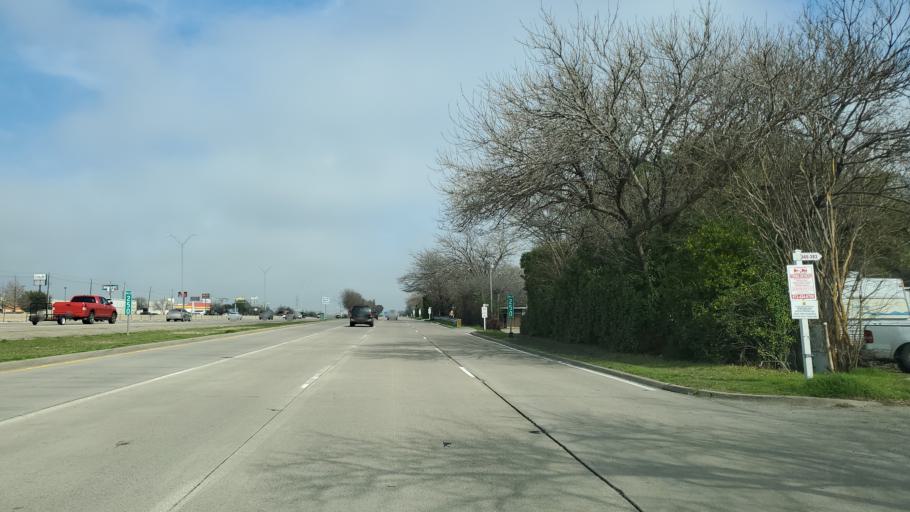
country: US
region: Texas
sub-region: Collin County
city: Plano
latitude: 33.0473
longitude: -96.6988
